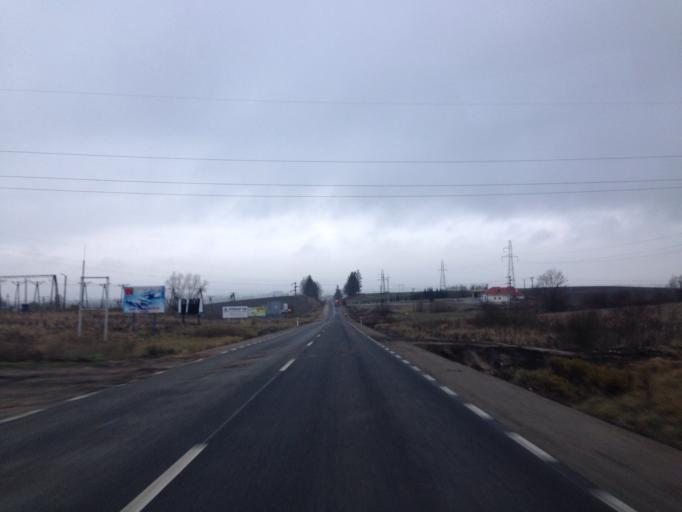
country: PL
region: Warmian-Masurian Voivodeship
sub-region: Powiat ketrzynski
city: Ketrzyn
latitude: 54.0678
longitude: 21.3656
